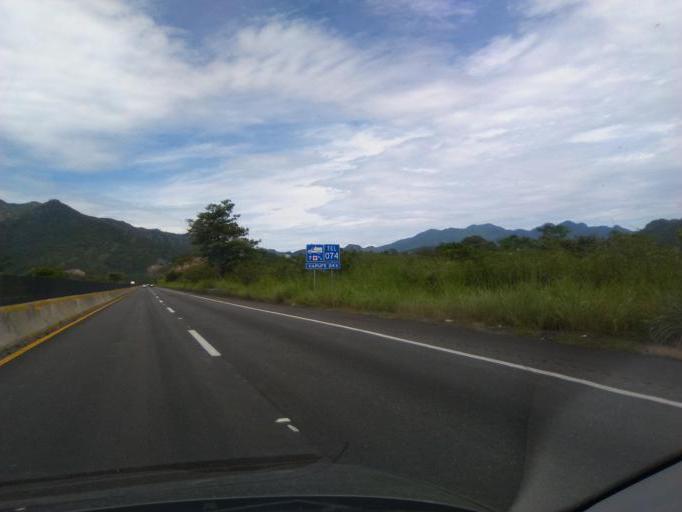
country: MX
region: Guerrero
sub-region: Chilpancingo de los Bravo
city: Cajelitos
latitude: 17.2773
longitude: -99.5087
